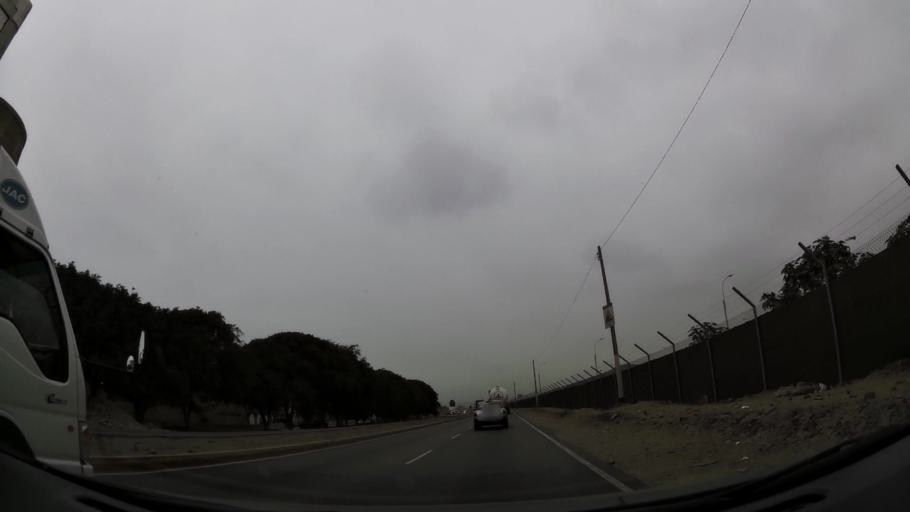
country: PE
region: Callao
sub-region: Callao
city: Callao
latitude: -12.0055
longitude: -77.1273
